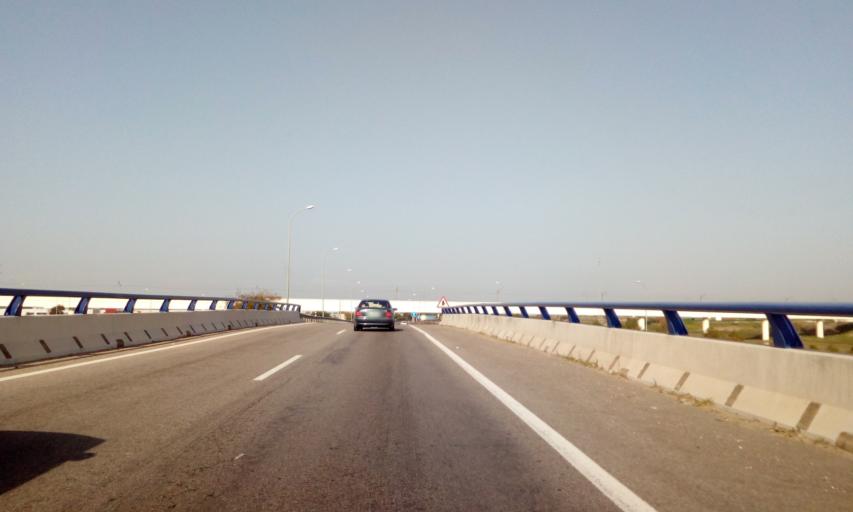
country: ES
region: Andalusia
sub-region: Provincia de Sevilla
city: Camas
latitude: 37.4137
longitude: -6.0319
